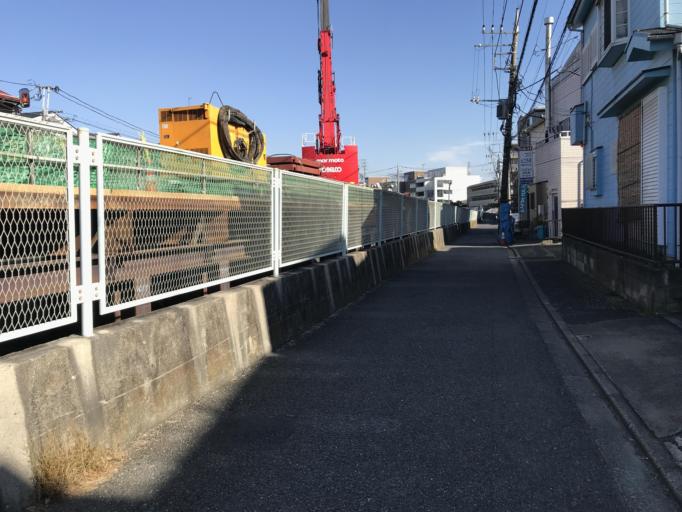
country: JP
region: Tokyo
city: Chofugaoka
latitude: 35.5986
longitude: 139.5948
